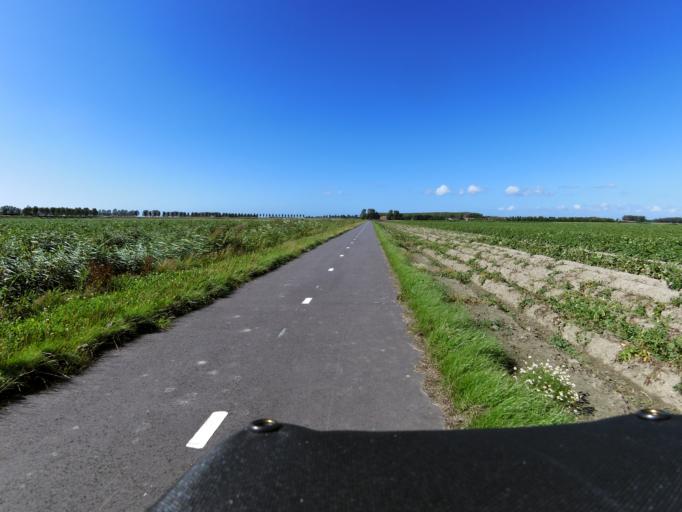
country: NL
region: South Holland
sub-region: Gemeente Goeree-Overflakkee
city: Dirksland
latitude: 51.7541
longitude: 4.0697
